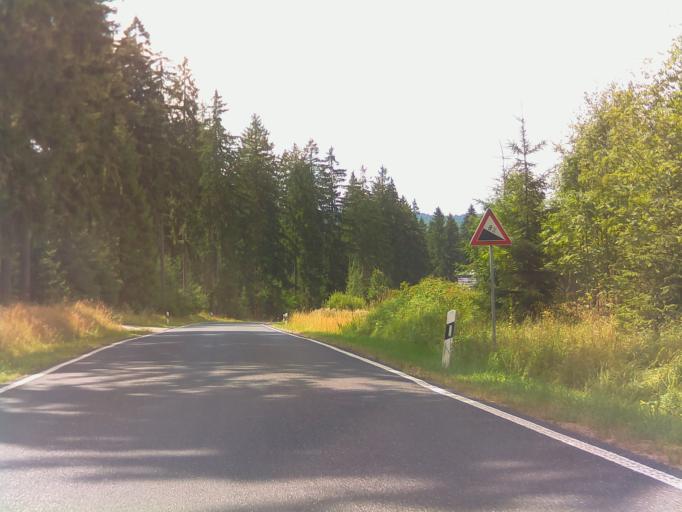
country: DE
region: Thuringia
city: Altenfeld
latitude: 50.5747
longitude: 10.9854
